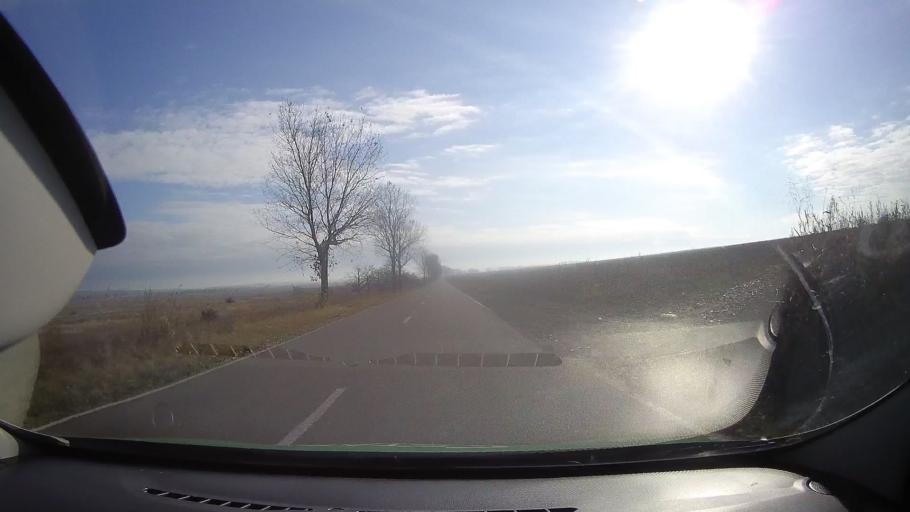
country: RO
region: Tulcea
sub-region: Comuna Mahmudia
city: Mahmudia
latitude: 45.0713
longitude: 29.0955
